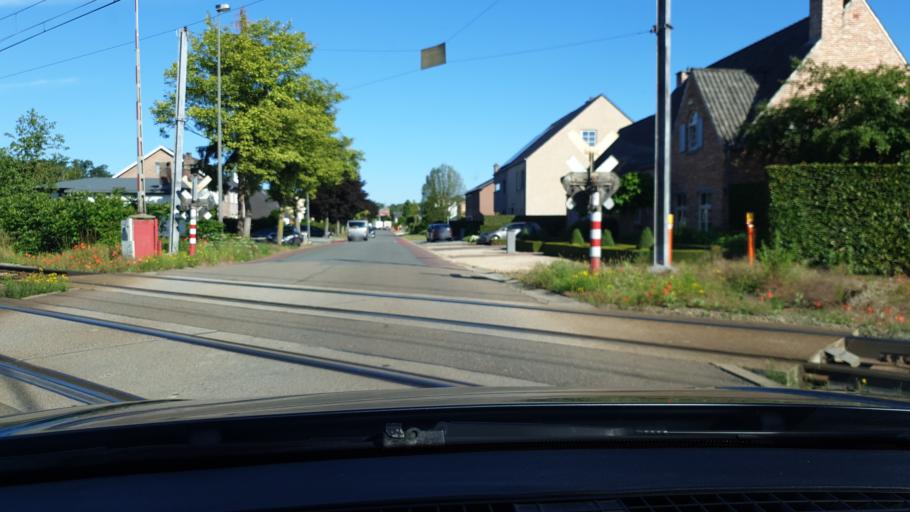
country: BE
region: Flanders
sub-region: Provincie Limburg
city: Hasselt
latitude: 50.9554
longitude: 5.3559
